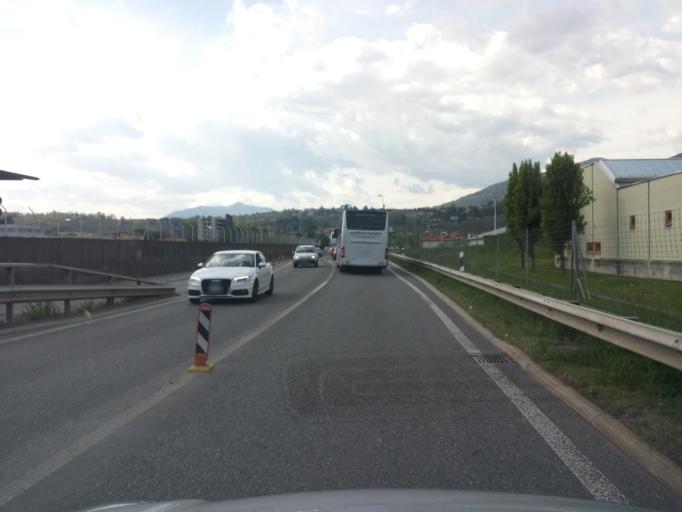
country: CH
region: Ticino
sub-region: Mendrisio District
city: Ligornetto
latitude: 45.8536
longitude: 8.9506
